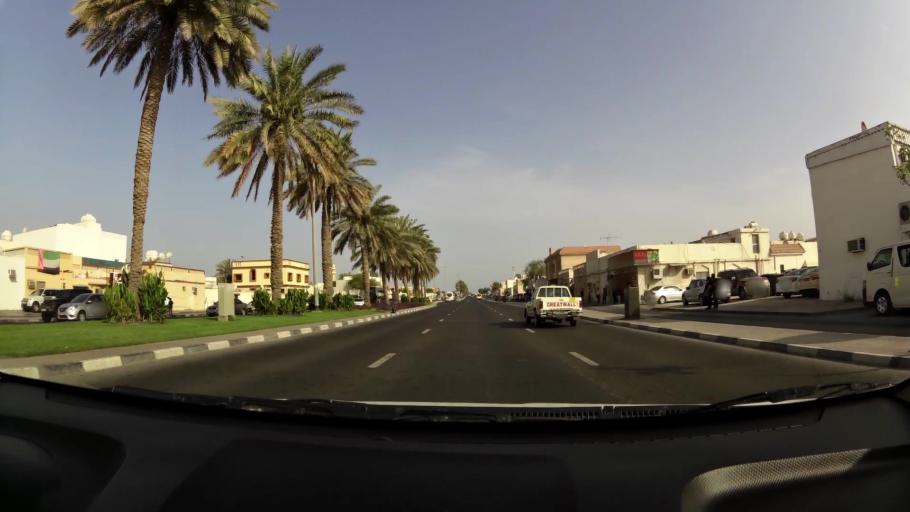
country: AE
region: Ash Shariqah
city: Sharjah
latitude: 25.2855
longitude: 55.3366
